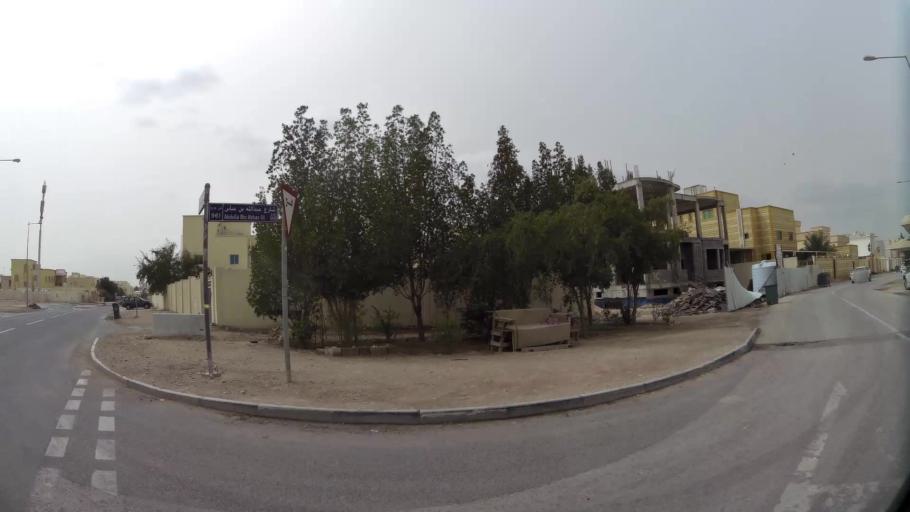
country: QA
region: Baladiyat ad Dawhah
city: Doha
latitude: 25.2400
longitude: 51.5299
